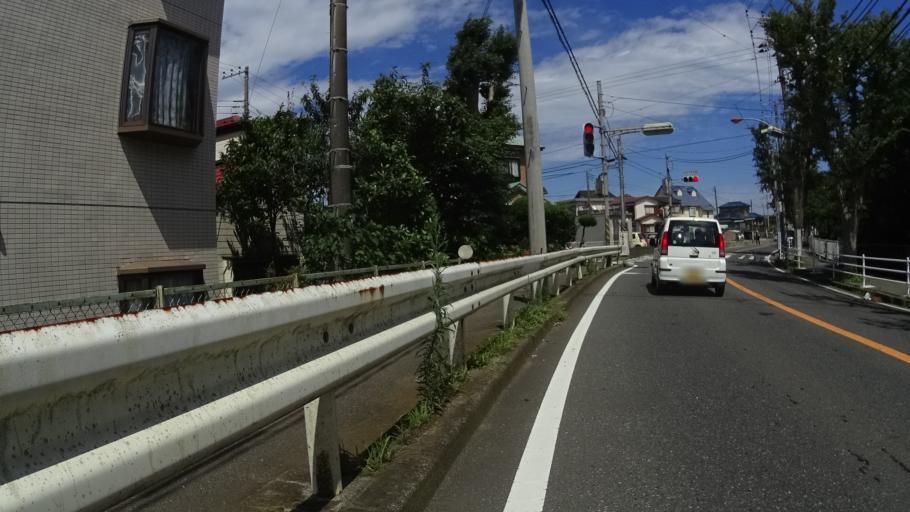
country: JP
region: Kanagawa
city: Miura
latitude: 35.1675
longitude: 139.6401
